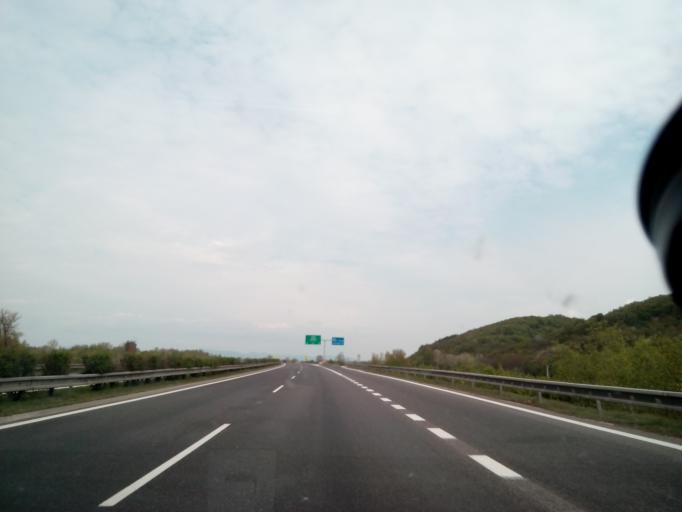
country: SK
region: Trnavsky
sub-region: Okres Trnava
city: Piestany
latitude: 48.6700
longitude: 17.8727
